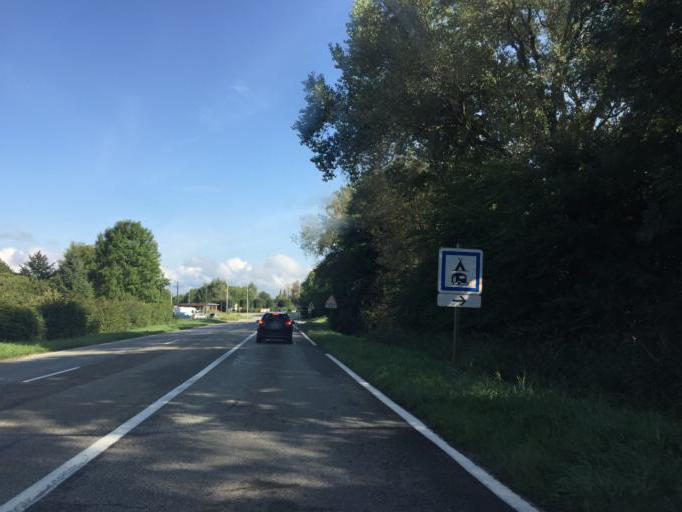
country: FR
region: Rhone-Alpes
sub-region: Departement de la Haute-Savoie
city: Beaumont
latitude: 46.0973
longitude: 6.1039
